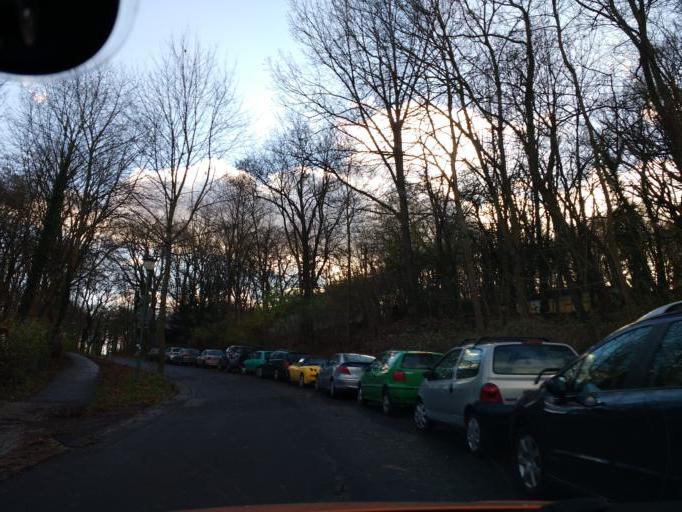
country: DE
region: Brandenburg
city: Potsdam
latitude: 52.3865
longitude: 13.0655
